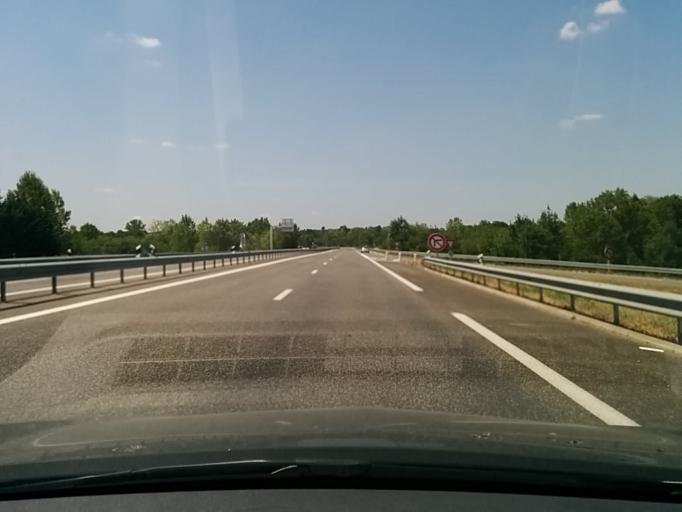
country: FR
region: Midi-Pyrenees
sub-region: Departement du Gers
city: Pujaudran
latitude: 43.6061
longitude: 1.0698
